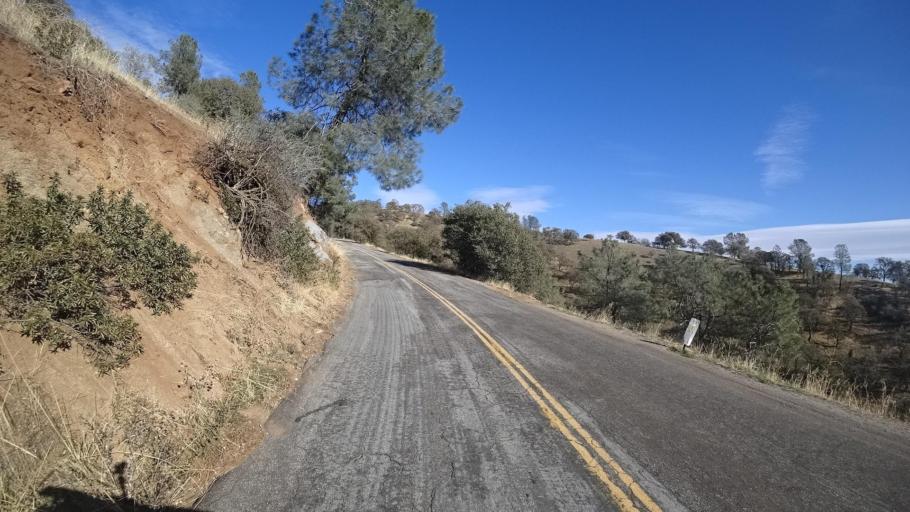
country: US
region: California
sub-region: Kern County
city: Bear Valley Springs
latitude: 35.3483
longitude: -118.5705
